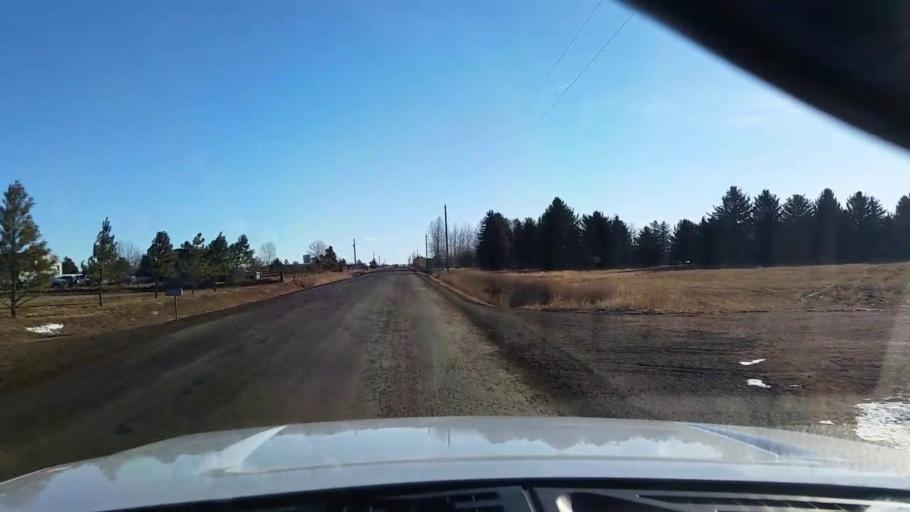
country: US
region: Colorado
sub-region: Larimer County
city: Wellington
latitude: 40.7696
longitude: -105.0866
